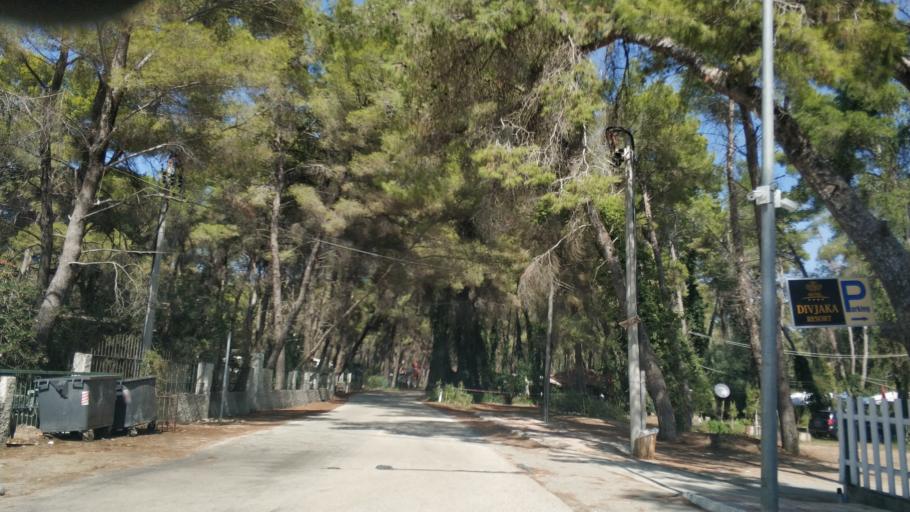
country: AL
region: Fier
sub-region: Rrethi i Lushnjes
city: Divjake
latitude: 40.9733
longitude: 19.4805
